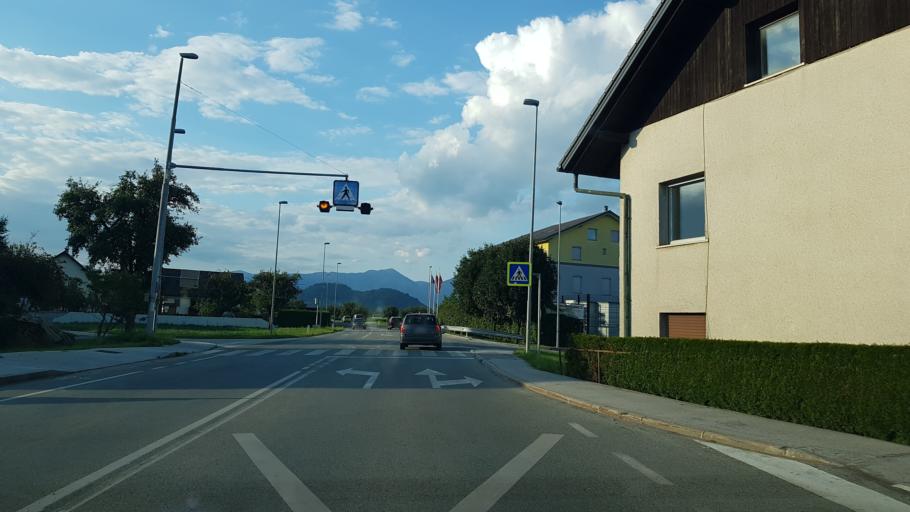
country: SI
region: Skofja Loka
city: Sv. Duh
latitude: 46.1967
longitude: 14.3323
